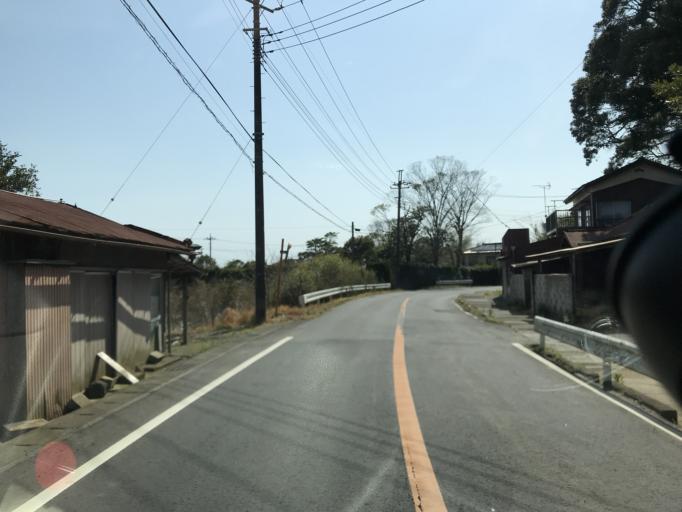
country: JP
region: Chiba
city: Yokaichiba
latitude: 35.7577
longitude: 140.5902
